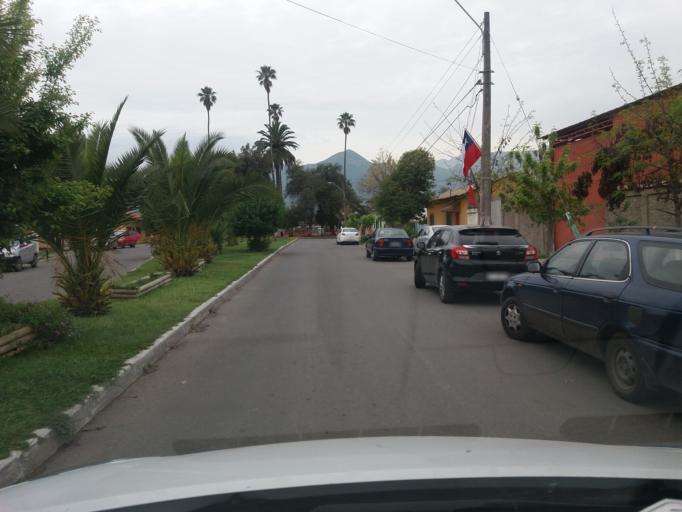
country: CL
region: Valparaiso
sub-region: Provincia de Quillota
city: Hacienda La Calera
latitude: -32.7788
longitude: -71.1849
